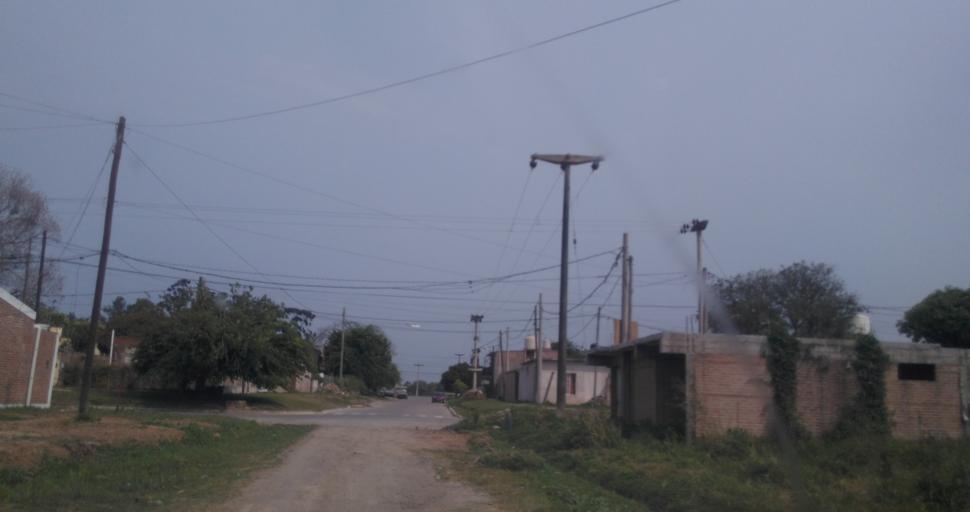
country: AR
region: Chaco
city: Fontana
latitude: -27.4266
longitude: -59.0258
